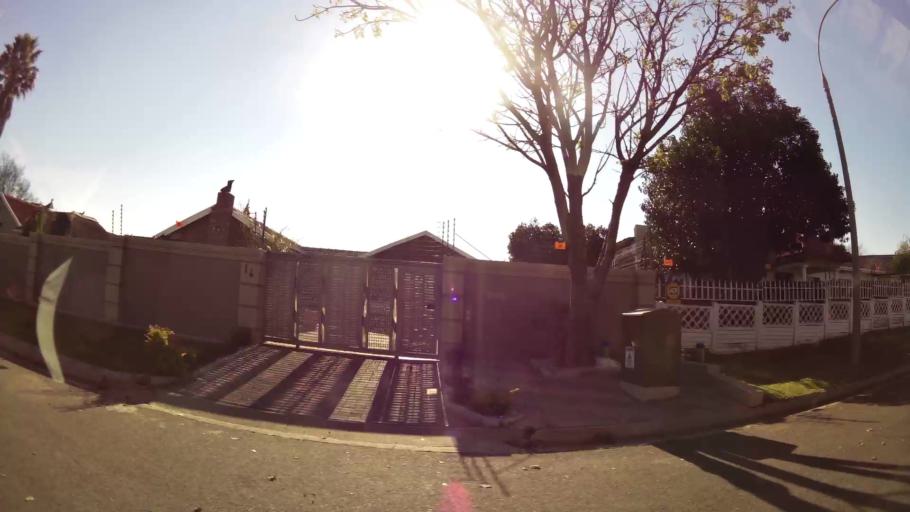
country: ZA
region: Gauteng
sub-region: City of Johannesburg Metropolitan Municipality
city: Modderfontein
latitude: -26.0567
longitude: 28.1990
